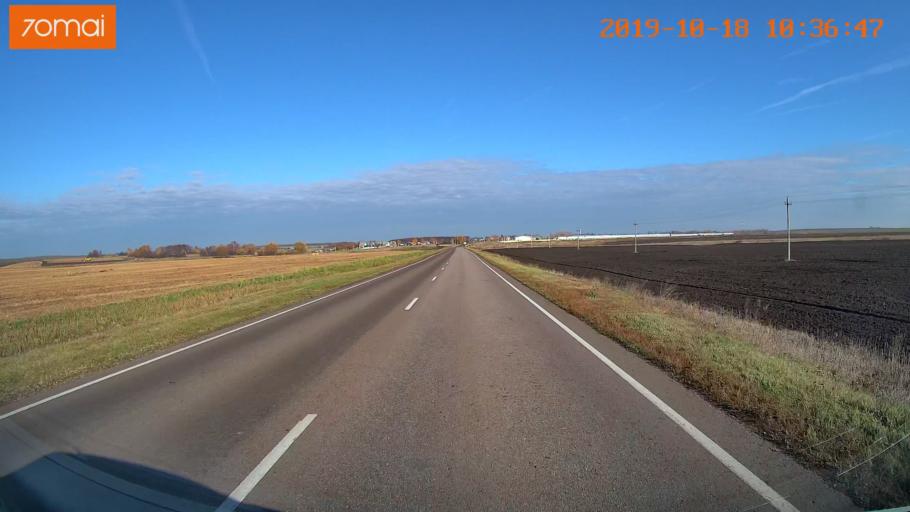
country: RU
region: Tula
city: Kurkino
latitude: 53.5534
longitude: 38.6275
